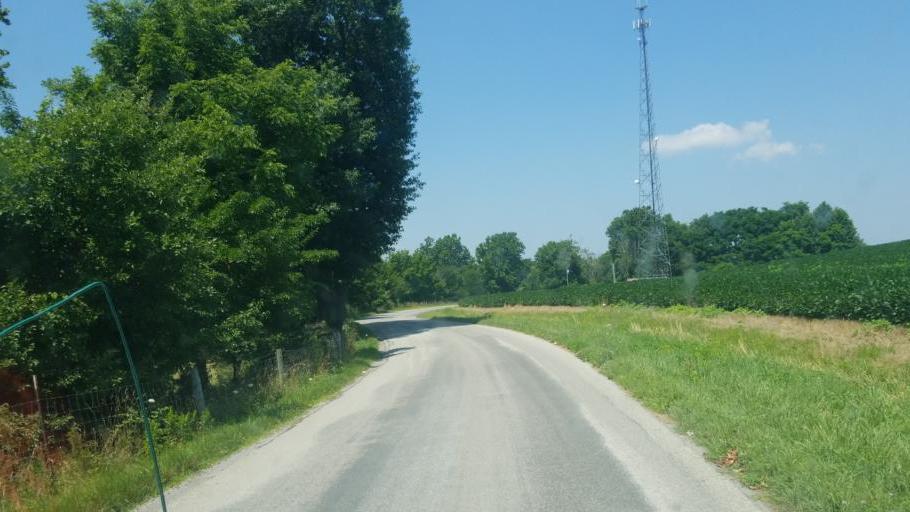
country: US
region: Ohio
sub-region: Richland County
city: Shelby
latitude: 40.8448
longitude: -82.6538
